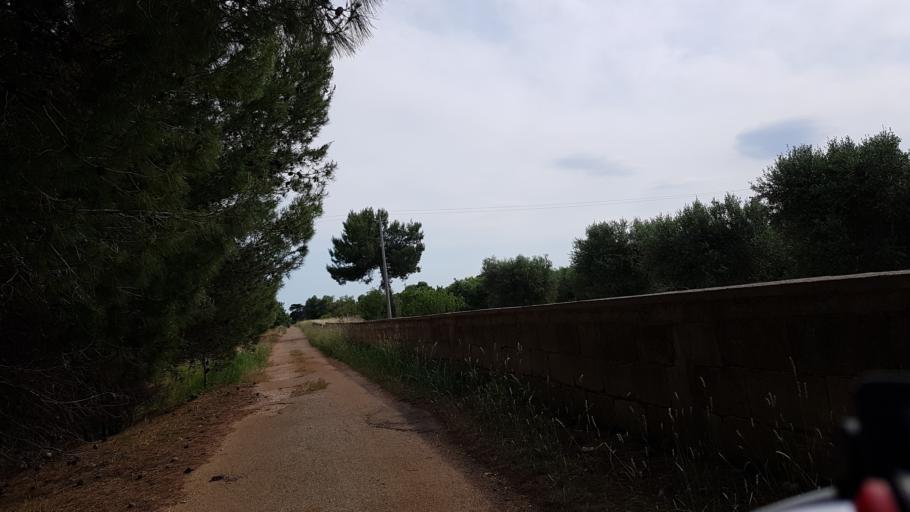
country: IT
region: Apulia
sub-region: Provincia di Brindisi
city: San Vito dei Normanni
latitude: 40.6512
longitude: 17.7711
